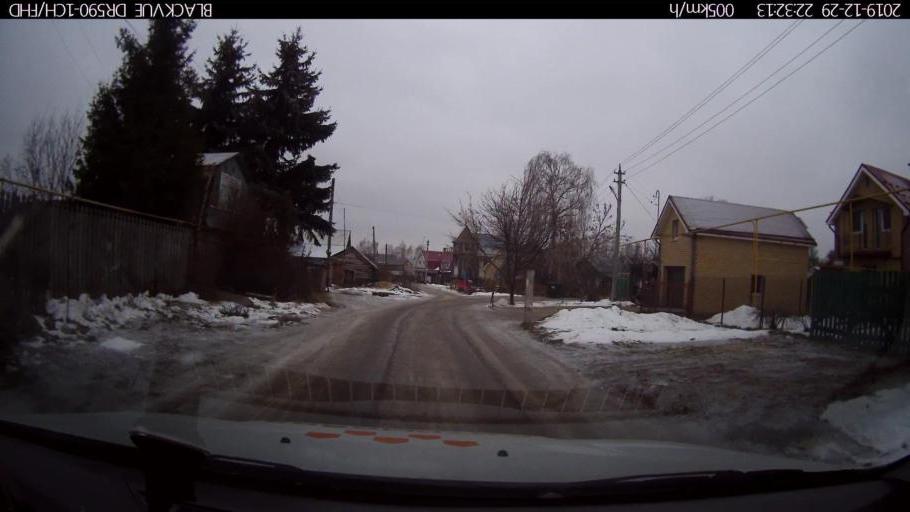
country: RU
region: Nizjnij Novgorod
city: Afonino
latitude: 56.2012
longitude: 43.9855
